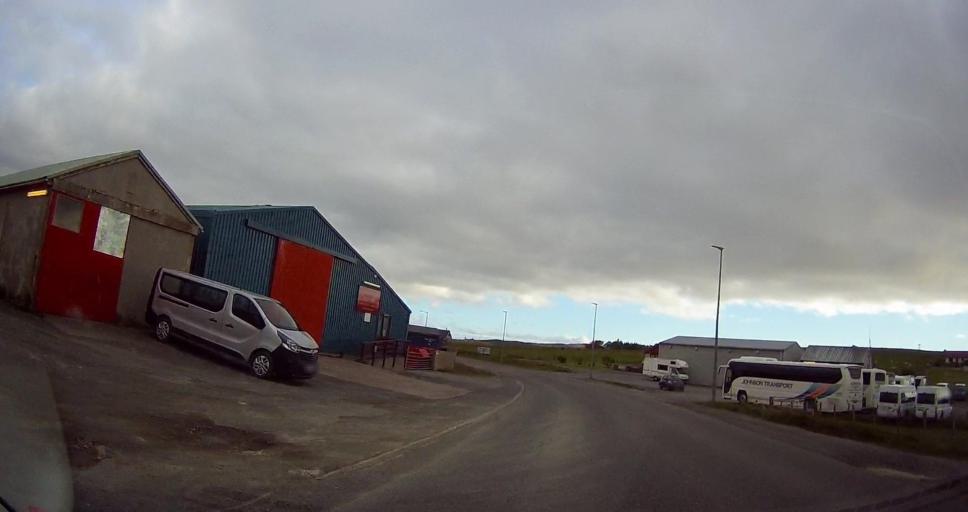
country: GB
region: Scotland
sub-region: Shetland Islands
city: Lerwick
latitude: 60.3986
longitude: -1.3532
